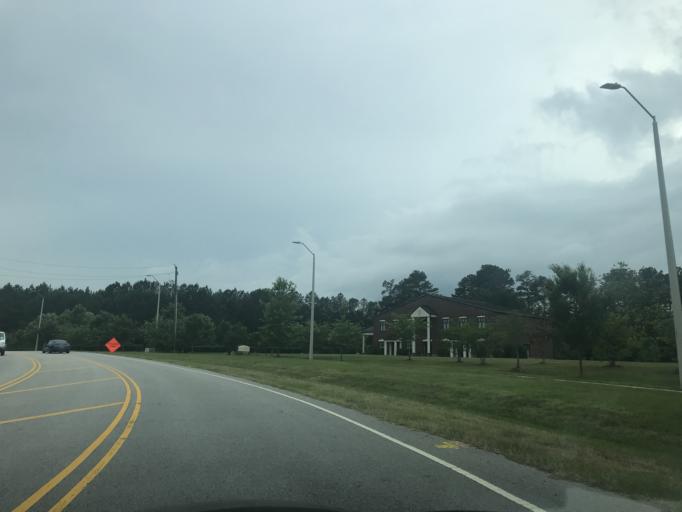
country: US
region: North Carolina
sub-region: Wake County
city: Green Level
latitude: 35.8056
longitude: -78.8884
